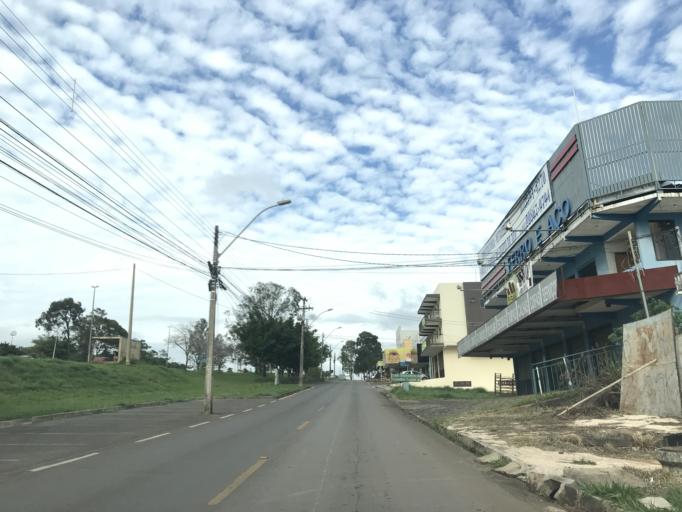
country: BR
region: Federal District
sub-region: Brasilia
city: Brasilia
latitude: -15.6574
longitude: -47.7888
